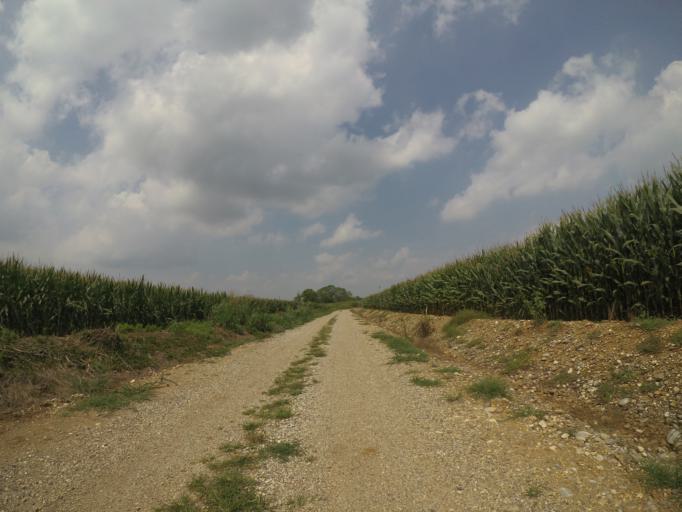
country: IT
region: Friuli Venezia Giulia
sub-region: Provincia di Udine
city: Codroipo
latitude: 45.9766
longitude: 13.0044
